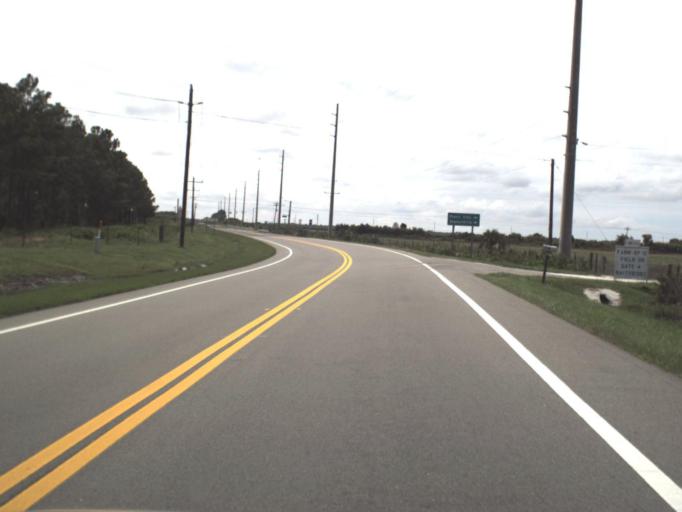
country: US
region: Florida
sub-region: Hillsborough County
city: Wimauma
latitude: 27.5895
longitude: -82.1499
